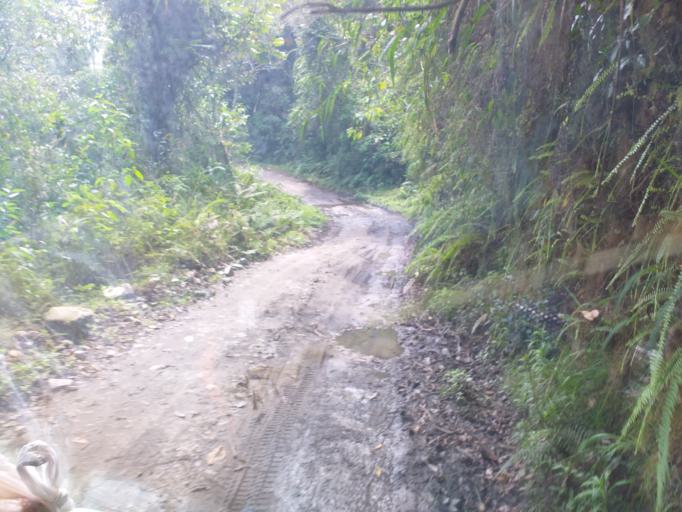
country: CO
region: Boyaca
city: Aquitania
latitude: 5.3350
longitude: -72.9319
